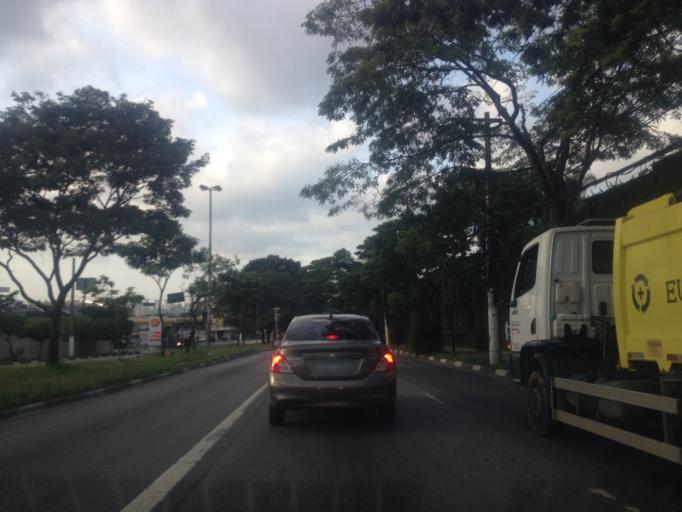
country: BR
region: Sao Paulo
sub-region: Diadema
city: Diadema
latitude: -23.6754
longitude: -46.7122
